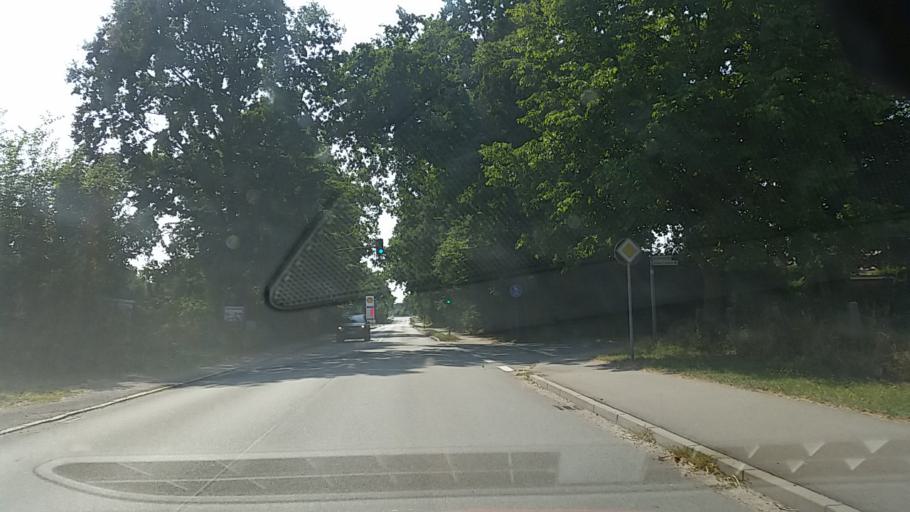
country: DE
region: Schleswig-Holstein
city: Witzhave
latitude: 53.5672
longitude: 10.3339
